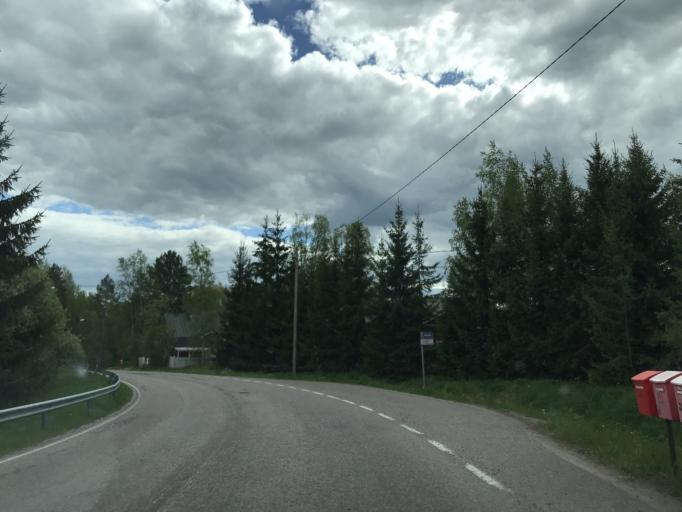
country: FI
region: Uusimaa
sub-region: Helsinki
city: Nurmijaervi
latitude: 60.4309
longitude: 24.7106
